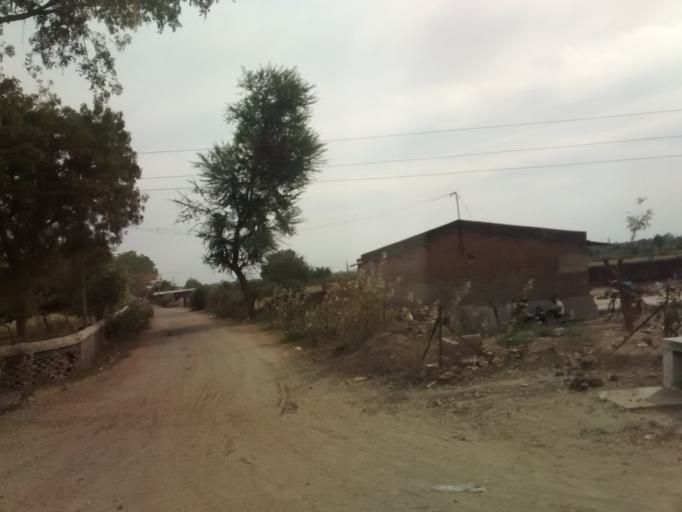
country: IN
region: Gujarat
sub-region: Gandhinagar
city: Ghandinagar
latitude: 23.2841
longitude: 72.6412
